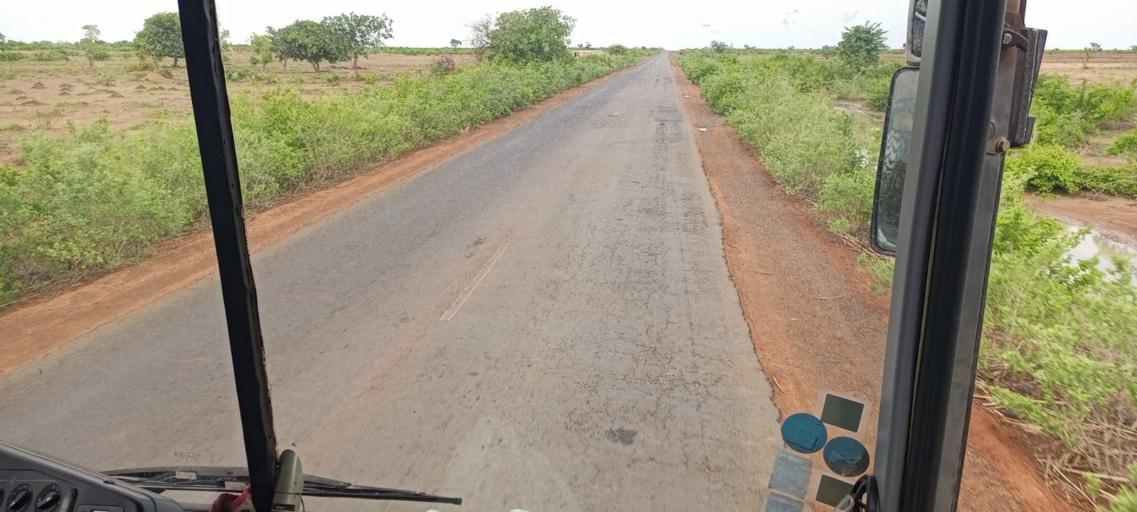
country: ML
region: Segou
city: Bla
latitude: 12.7095
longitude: -5.7244
